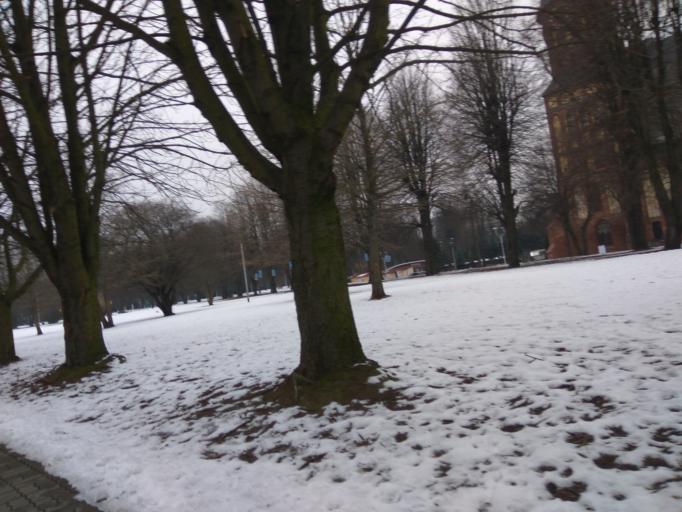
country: RU
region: Kaliningrad
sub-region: Gorod Kaliningrad
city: Kaliningrad
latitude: 54.7056
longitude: 20.5118
